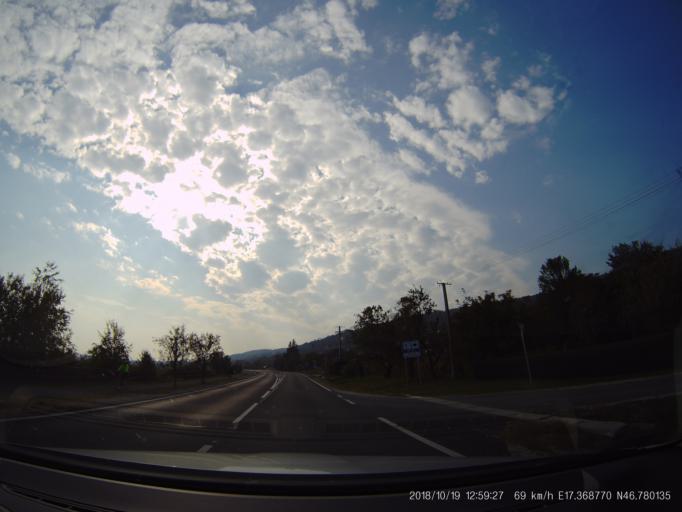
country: HU
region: Zala
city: Vonyarcvashegy
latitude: 46.7801
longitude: 17.3687
